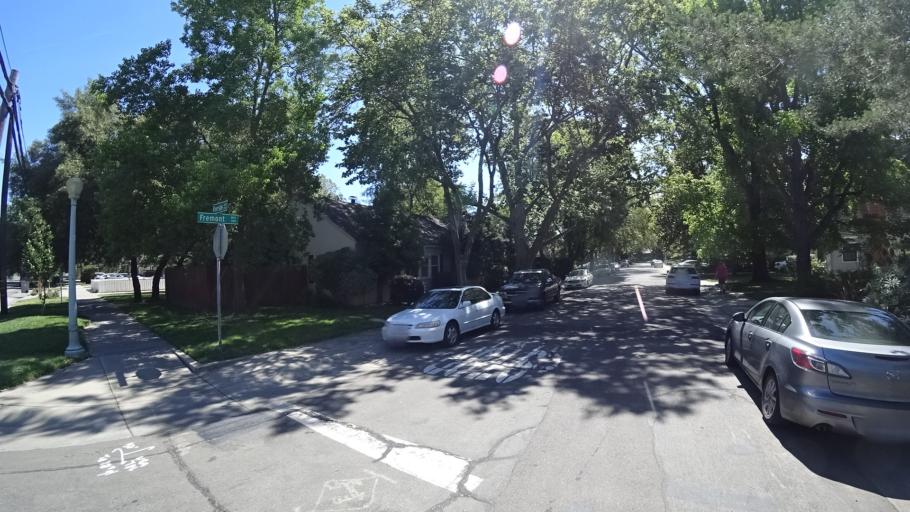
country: US
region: California
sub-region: Sacramento County
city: Sacramento
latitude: 38.5571
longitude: -121.5017
